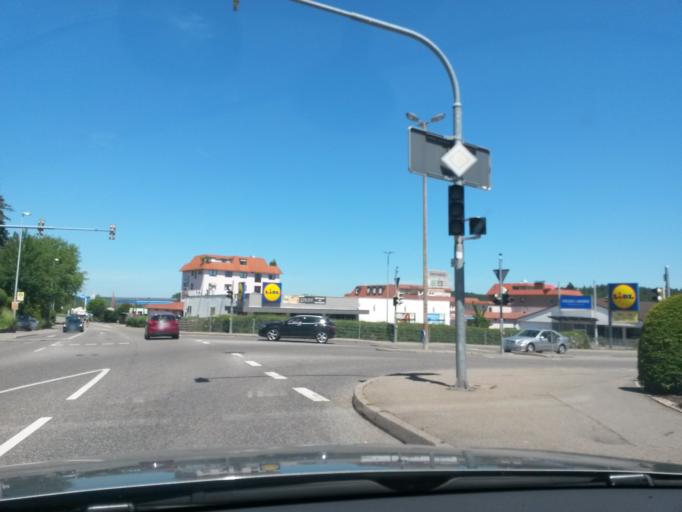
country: DE
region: Baden-Wuerttemberg
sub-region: Regierungsbezirk Stuttgart
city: Weil der Stadt
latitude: 48.7550
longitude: 8.8685
